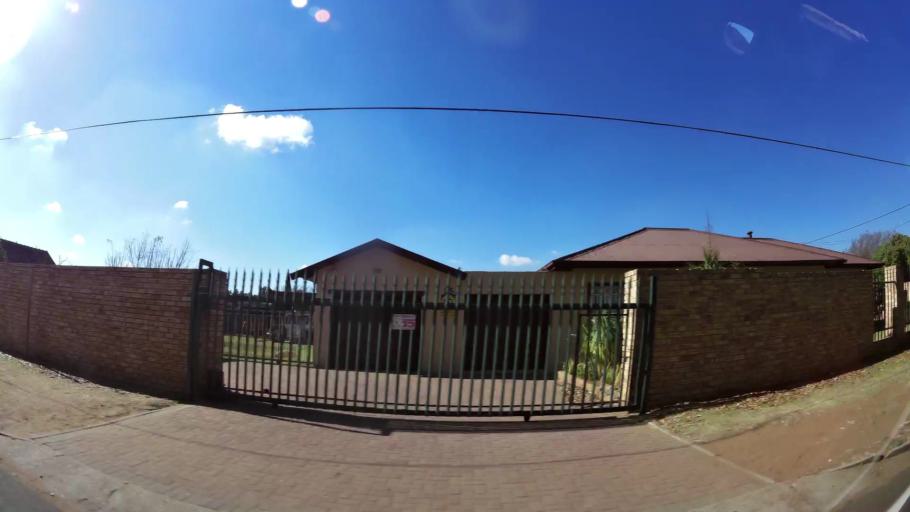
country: ZA
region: Gauteng
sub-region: City of Johannesburg Metropolitan Municipality
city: Roodepoort
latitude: -26.1357
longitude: 27.8341
